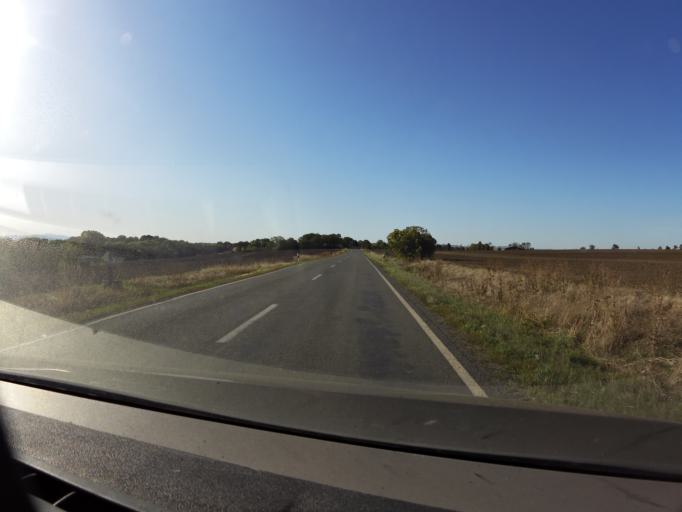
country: DE
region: Saxony-Anhalt
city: Hedersleben
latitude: 51.8756
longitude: 11.2291
